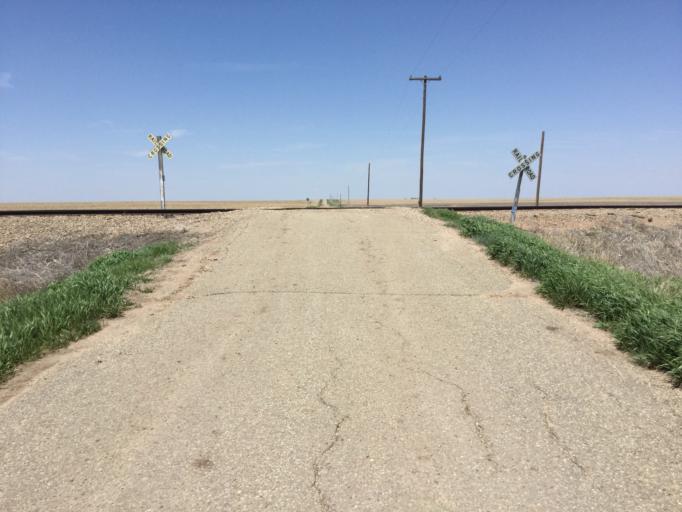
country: US
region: Kansas
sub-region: Decatur County
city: Oberlin
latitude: 39.6273
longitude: -100.4047
